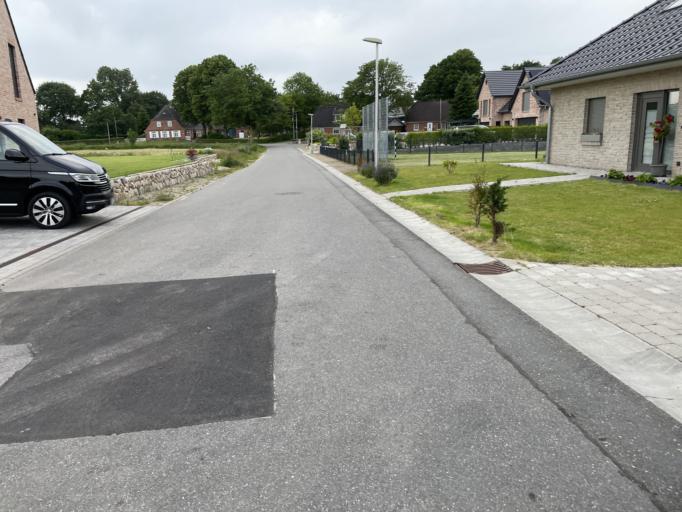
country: DE
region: Schleswig-Holstein
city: Mildstedt
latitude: 54.4586
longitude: 9.0927
